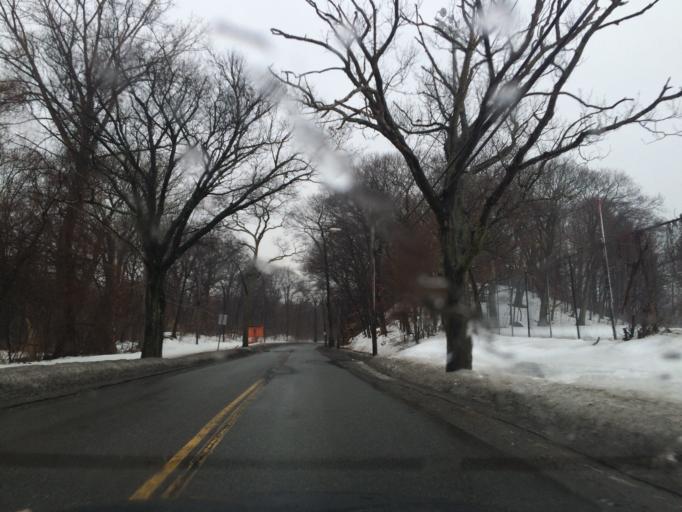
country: US
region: Massachusetts
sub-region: Middlesex County
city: Waltham
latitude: 42.3832
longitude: -71.2109
